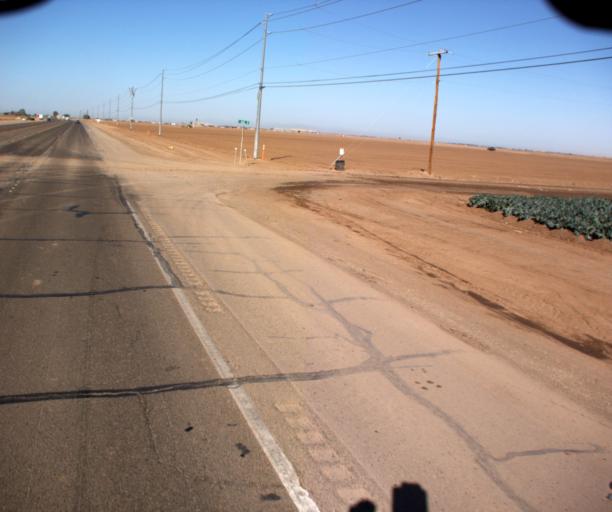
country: US
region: Arizona
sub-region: Yuma County
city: Somerton
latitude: 32.5967
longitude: -114.7523
